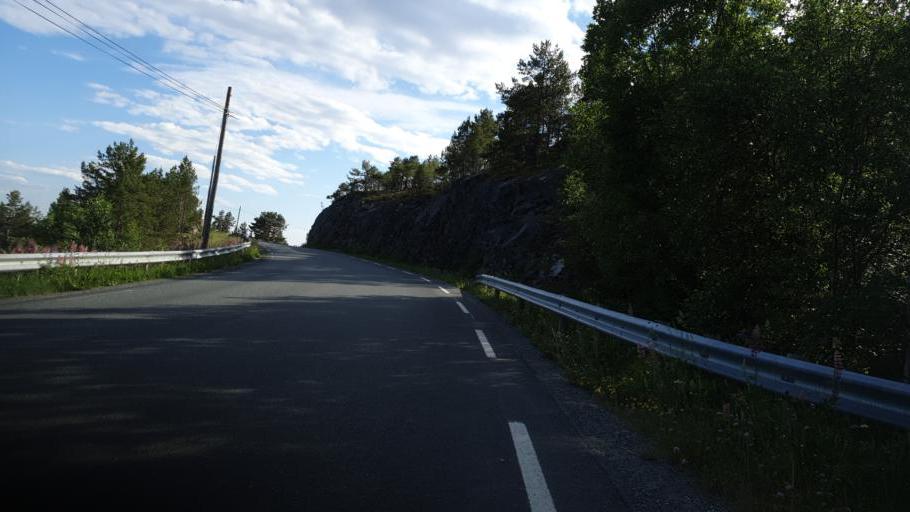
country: NO
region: Sor-Trondelag
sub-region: Trondheim
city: Trondheim
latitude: 63.5687
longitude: 10.3422
